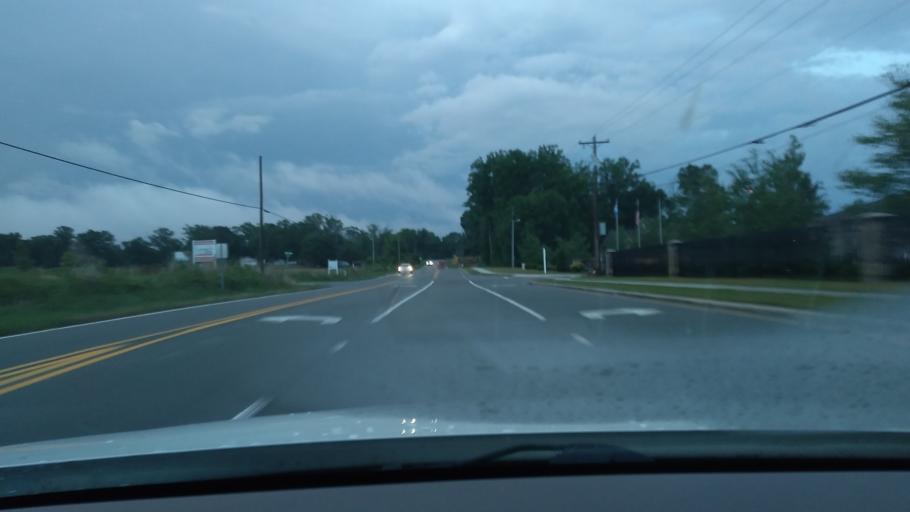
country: US
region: North Carolina
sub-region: Guilford County
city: McLeansville
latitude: 36.0617
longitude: -79.7004
